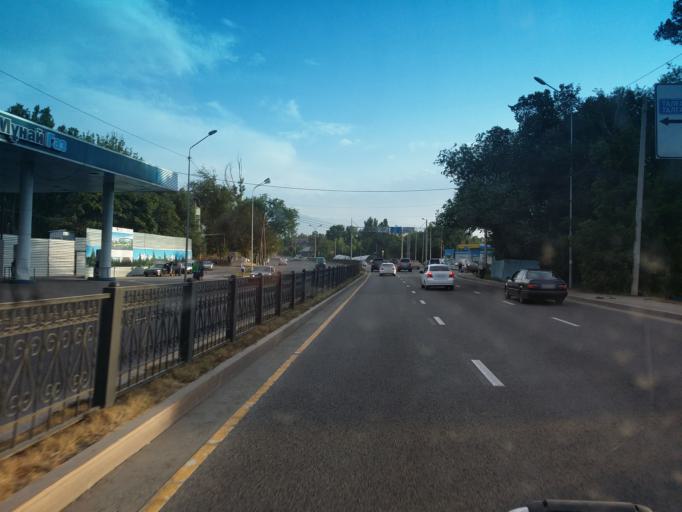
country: KZ
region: Almaty Qalasy
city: Almaty
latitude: 43.2886
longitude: 76.9891
